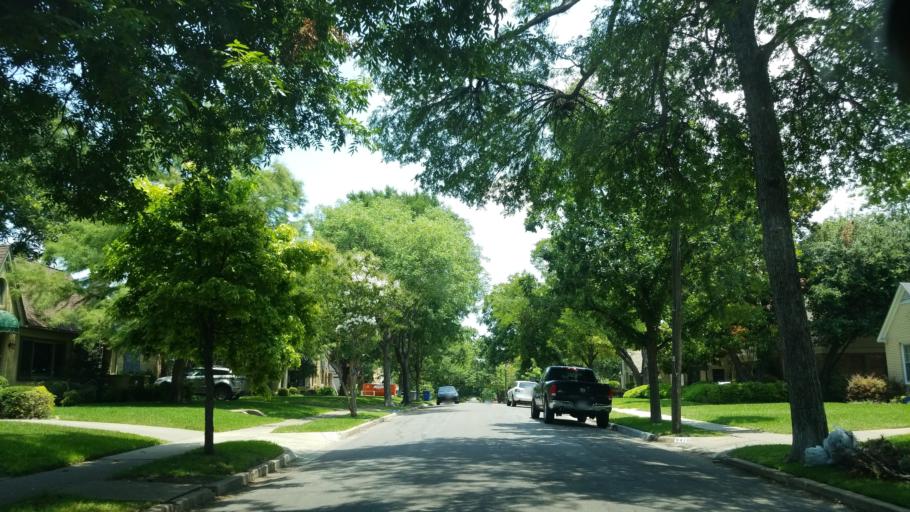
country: US
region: Texas
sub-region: Dallas County
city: Highland Park
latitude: 32.8291
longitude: -96.7766
